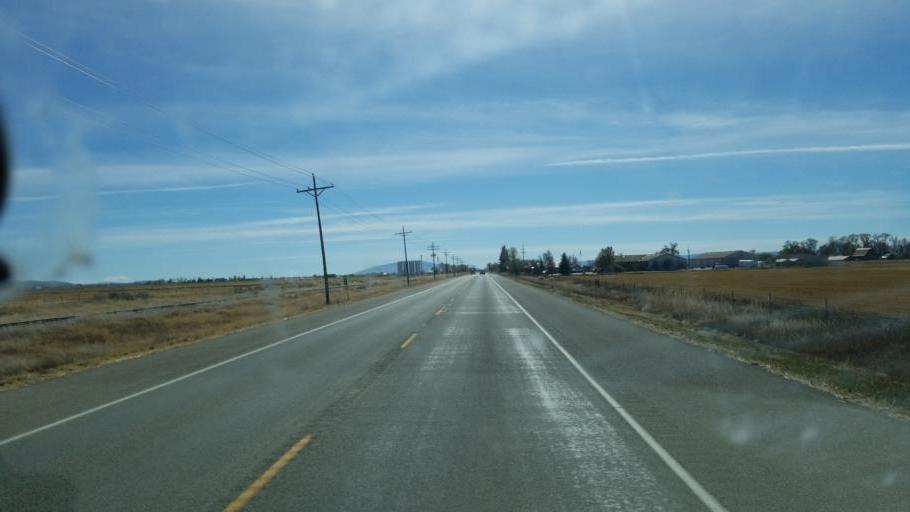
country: US
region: Colorado
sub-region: Conejos County
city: Conejos
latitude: 37.2353
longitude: -105.9717
